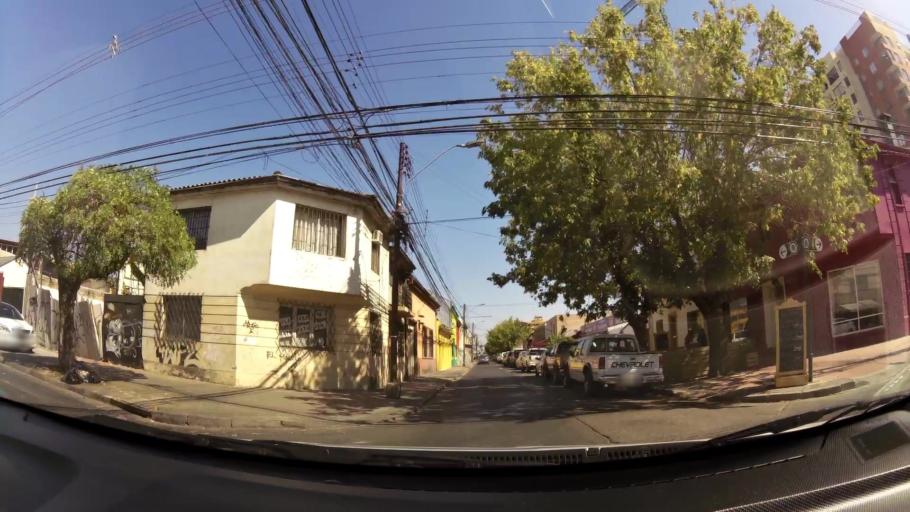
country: CL
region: Maule
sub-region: Provincia de Talca
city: Talca
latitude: -35.4298
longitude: -71.6600
